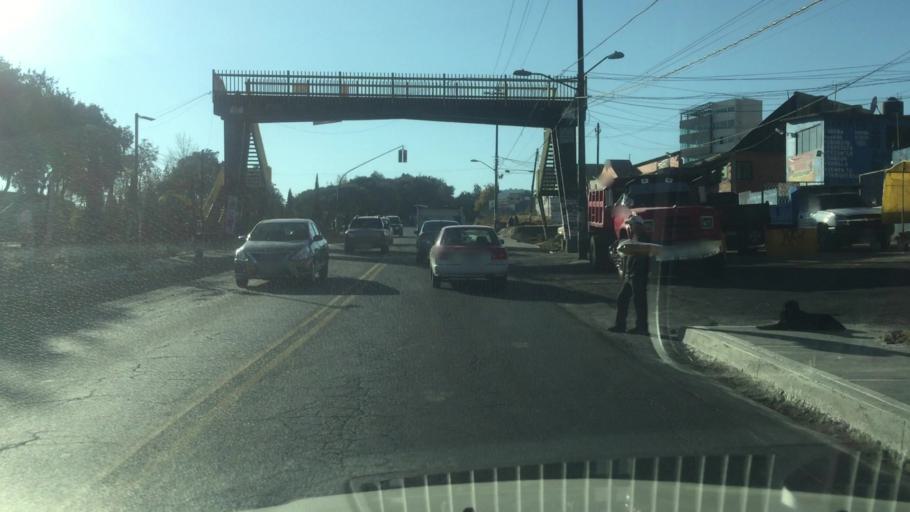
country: MX
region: Mexico City
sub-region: Tlalpan
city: Lomas de Tepemecatl
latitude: 19.2681
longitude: -99.2052
